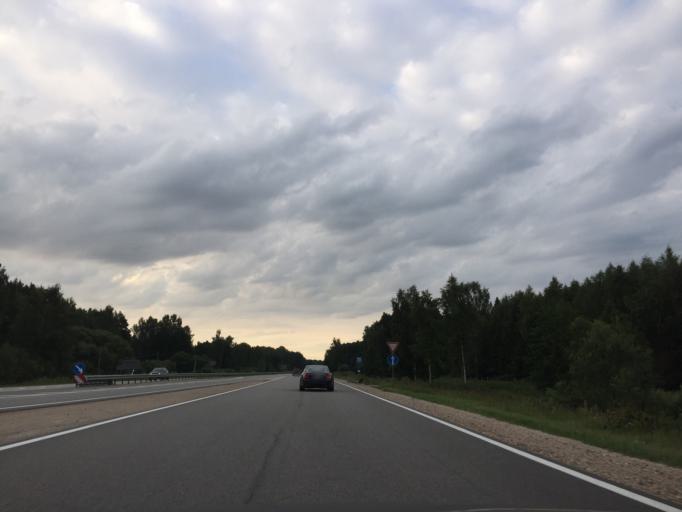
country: LV
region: Babite
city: Pinki
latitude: 56.9276
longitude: 23.9159
